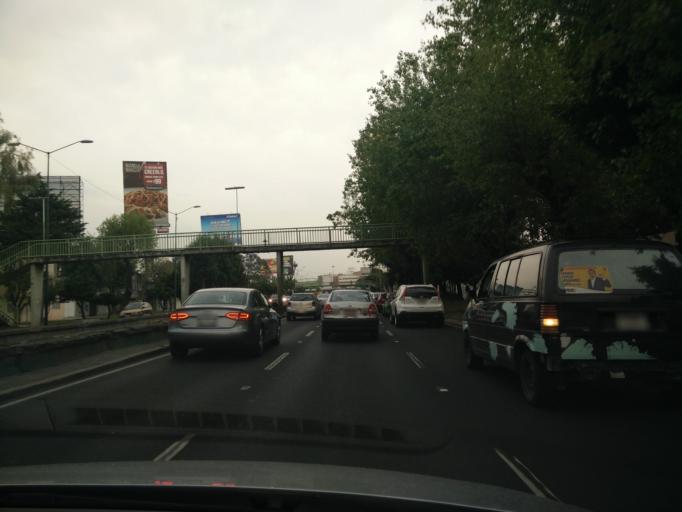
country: MX
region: Mexico City
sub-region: Iztacalco
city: Iztacalco
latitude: 19.4055
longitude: -99.1184
